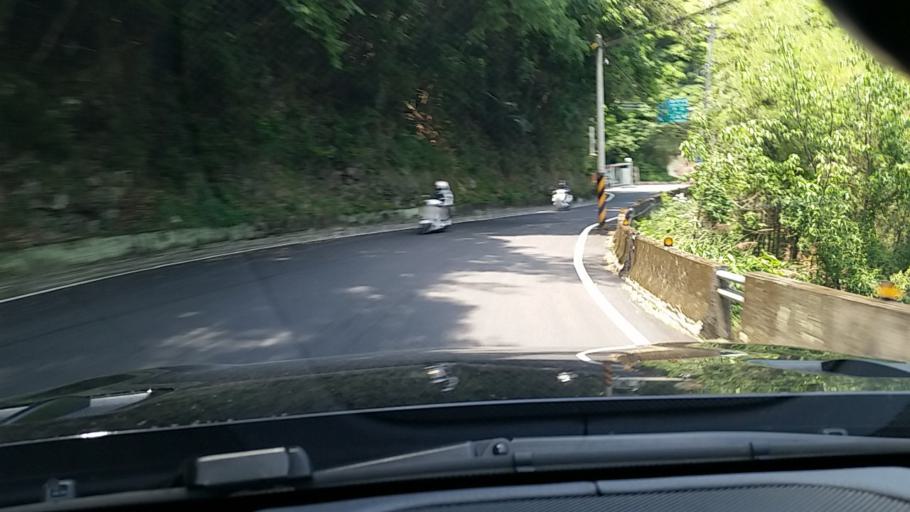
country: TW
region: Taiwan
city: Daxi
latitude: 24.7097
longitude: 121.3613
